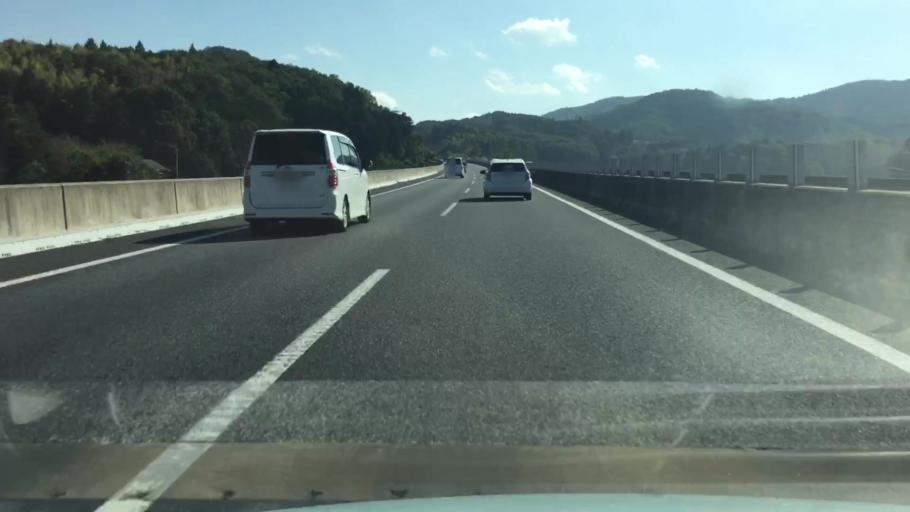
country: JP
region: Ibaraki
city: Iwase
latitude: 36.3429
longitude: 140.1862
